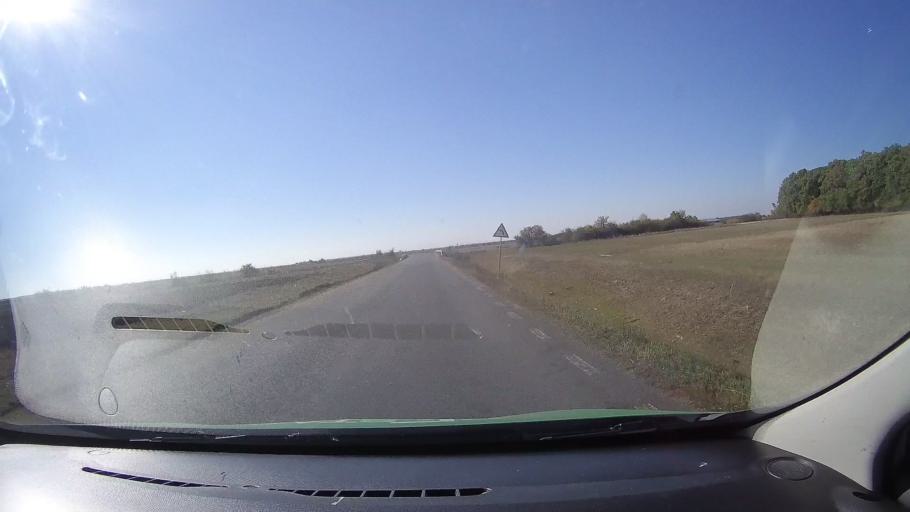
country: RO
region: Satu Mare
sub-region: Municipiul Satu Mare
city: Satmarel
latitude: 47.7005
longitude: 22.7715
